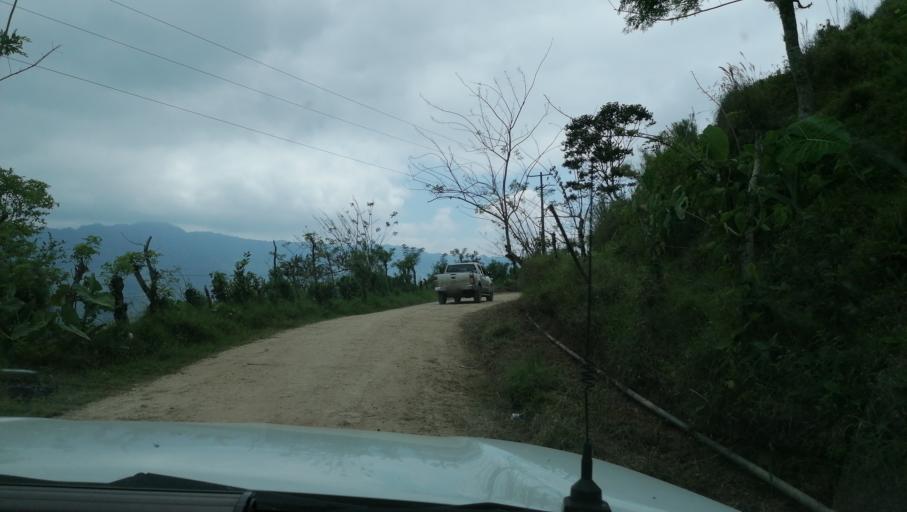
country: MX
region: Chiapas
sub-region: Ocotepec
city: San Pablo Huacano
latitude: 17.2677
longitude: -93.2524
